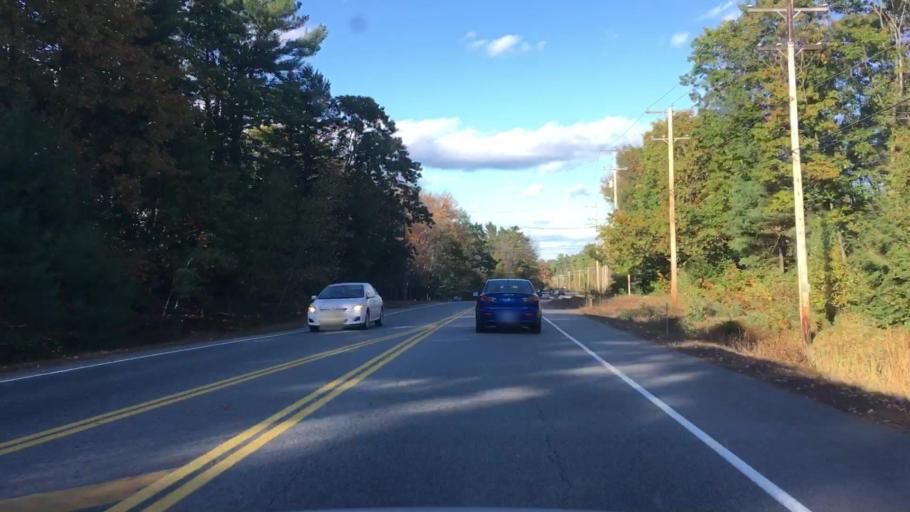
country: US
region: Maine
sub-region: Cumberland County
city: West Scarborough
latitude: 43.6098
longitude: -70.3607
